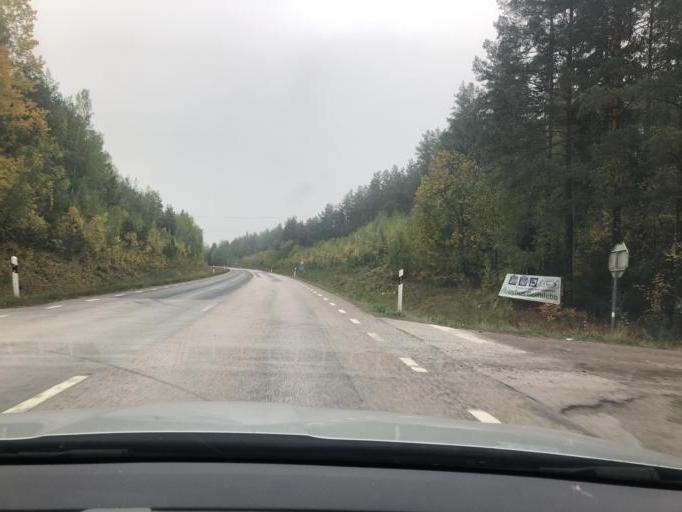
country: SE
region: Uppsala
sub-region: Tierps Kommun
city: Orbyhus
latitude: 60.2237
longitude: 17.6838
